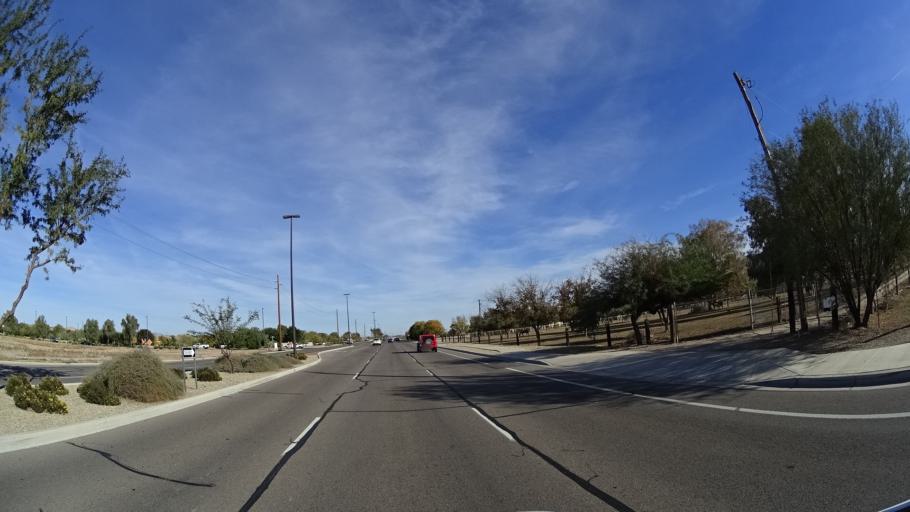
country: US
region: Arizona
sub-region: Maricopa County
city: Queen Creek
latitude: 33.2192
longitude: -111.7525
